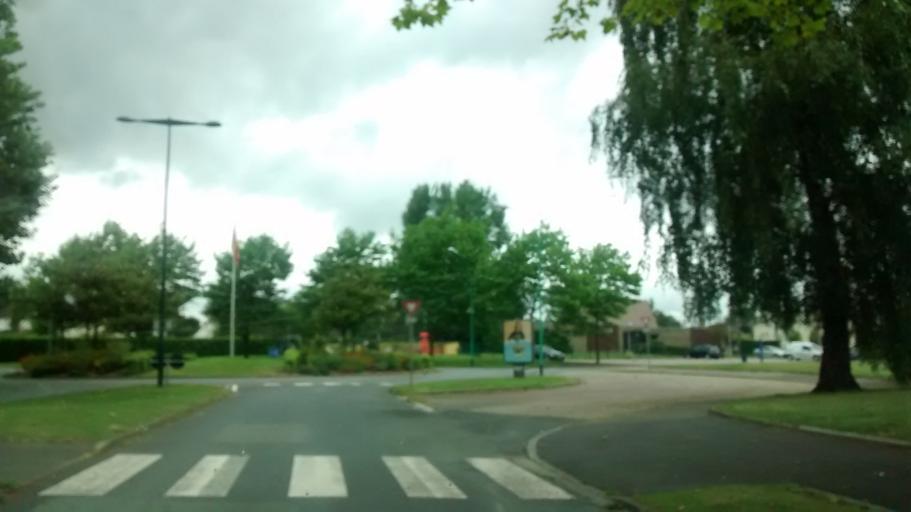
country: FR
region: Haute-Normandie
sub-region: Departement de la Seine-Maritime
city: Bois-Guillaume
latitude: 49.4699
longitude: 1.1414
